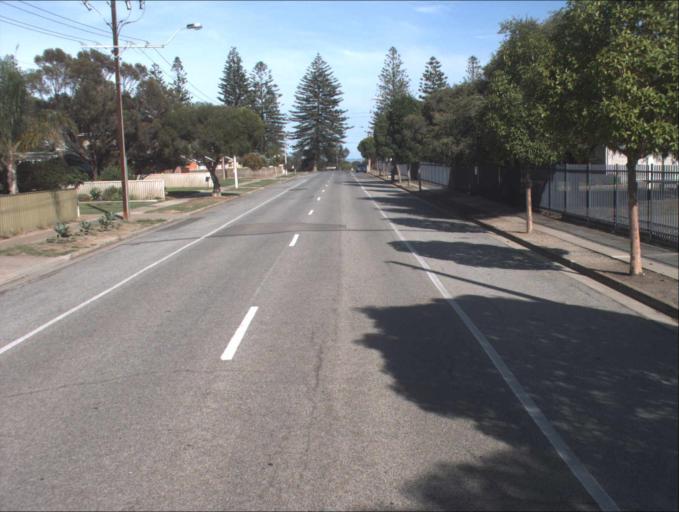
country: AU
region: South Australia
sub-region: Port Adelaide Enfield
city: Birkenhead
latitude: -34.8043
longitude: 138.4937
